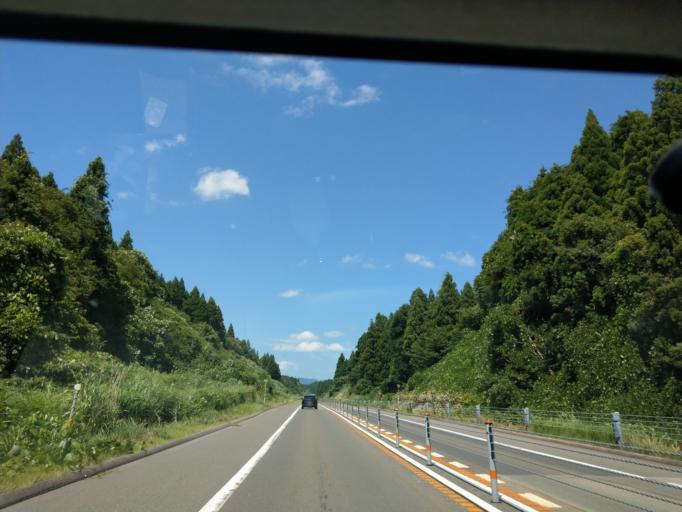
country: JP
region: Akita
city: Akita
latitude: 39.6878
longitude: 140.1858
